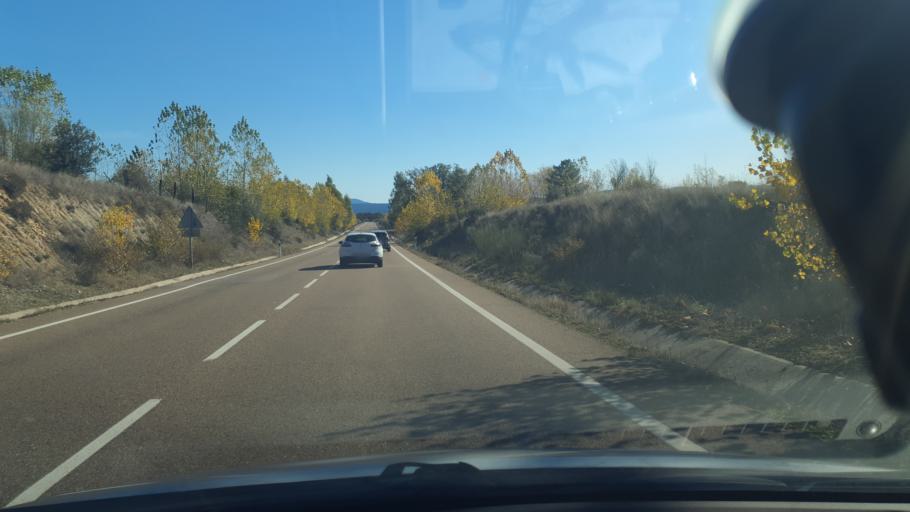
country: ES
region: Castille and Leon
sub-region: Provincia de Avila
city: Arenas de San Pedro
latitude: 40.1887
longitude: -5.0661
